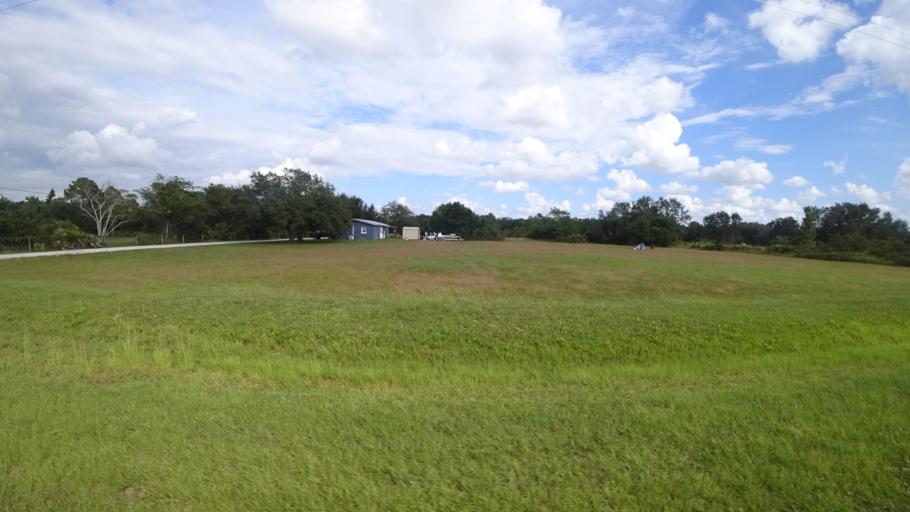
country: US
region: Florida
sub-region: Hillsborough County
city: Wimauma
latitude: 27.5876
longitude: -82.1988
